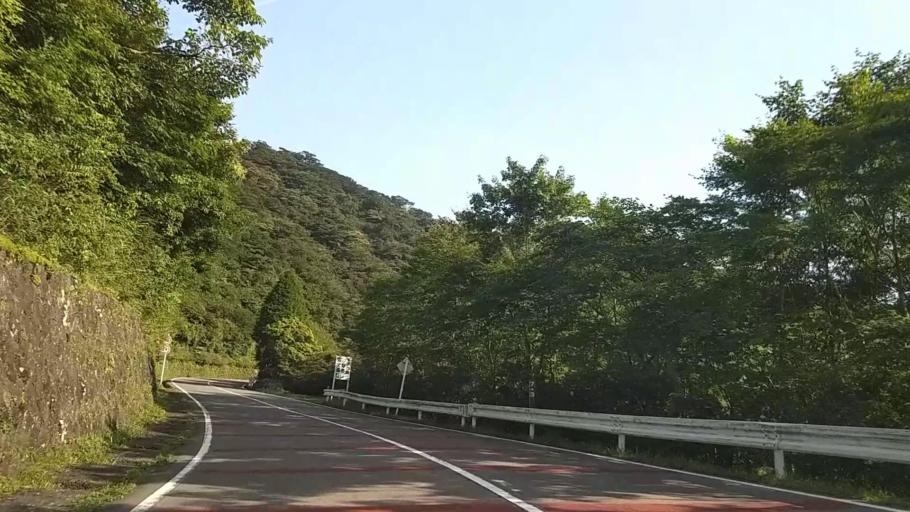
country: JP
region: Kanagawa
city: Hakone
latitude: 35.2197
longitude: 138.9806
